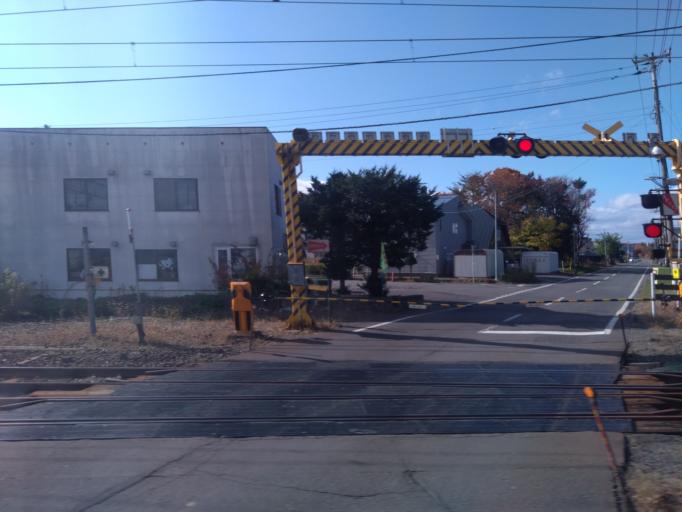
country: JP
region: Hokkaido
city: Kitahiroshima
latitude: 42.9238
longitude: 141.5731
